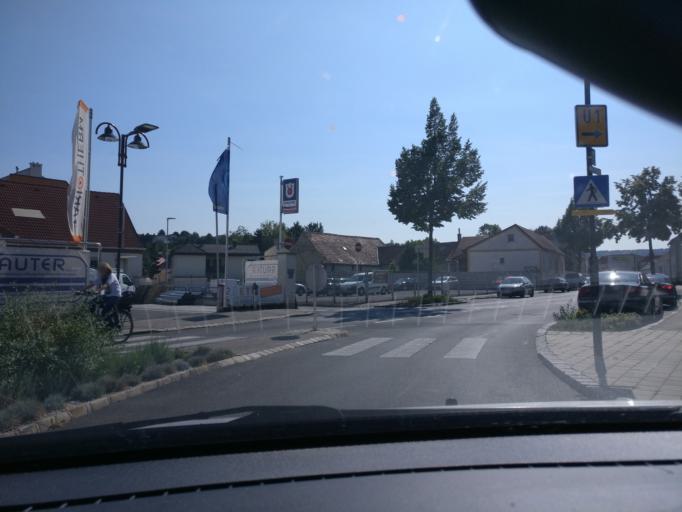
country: AT
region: Burgenland
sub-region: Politischer Bezirk Mattersburg
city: Mattersburg
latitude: 47.7374
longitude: 16.3964
